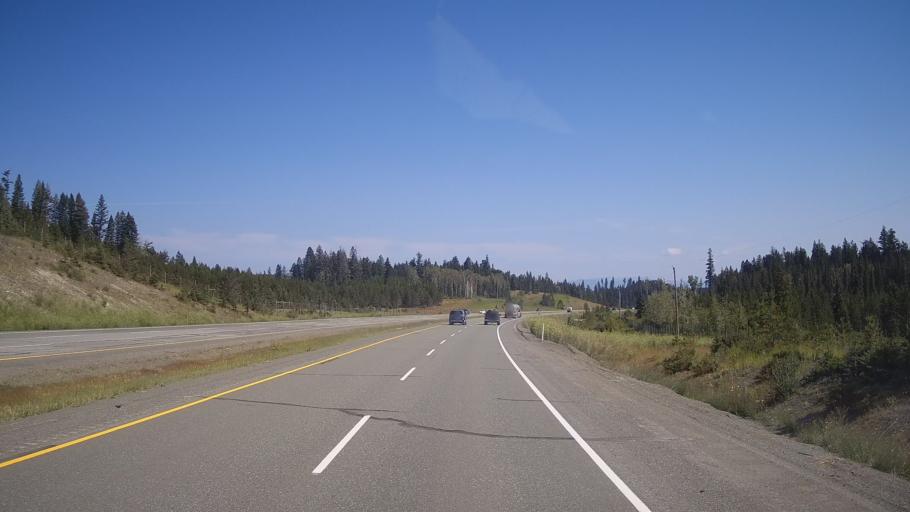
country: CA
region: British Columbia
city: Kamloops
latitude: 50.5319
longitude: -120.4778
